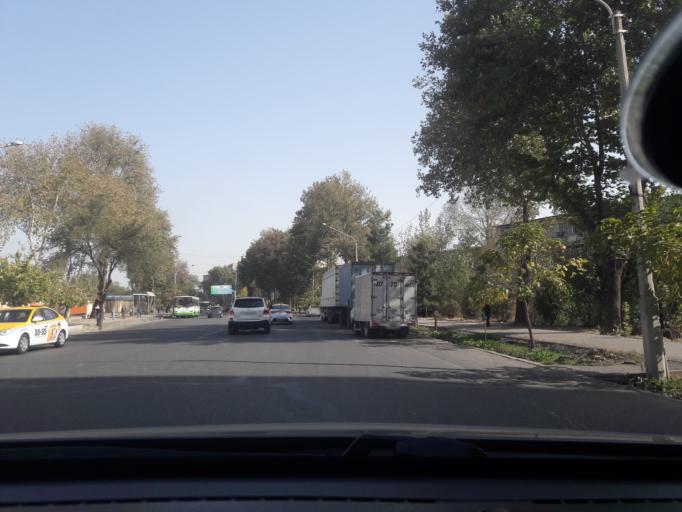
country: TJ
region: Dushanbe
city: Dushanbe
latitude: 38.5181
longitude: 68.7520
